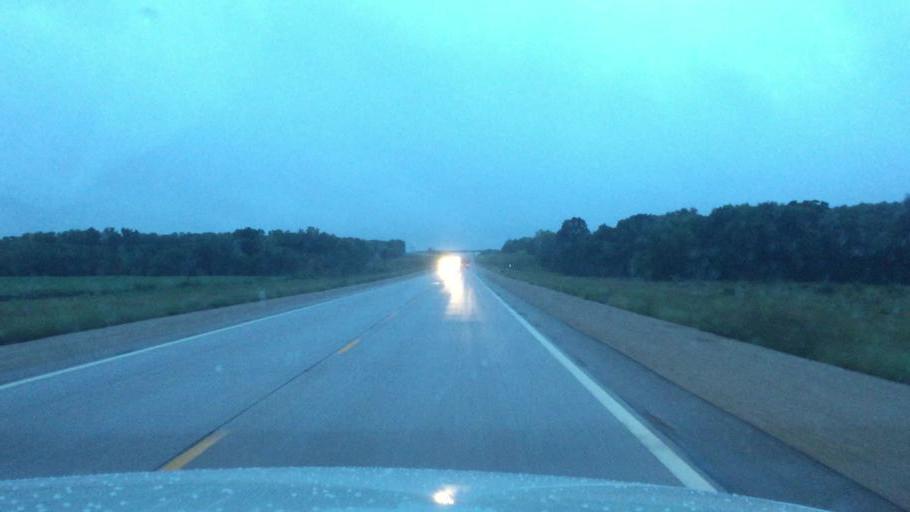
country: US
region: Kansas
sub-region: Allen County
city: Humboldt
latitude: 37.8011
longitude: -95.4114
